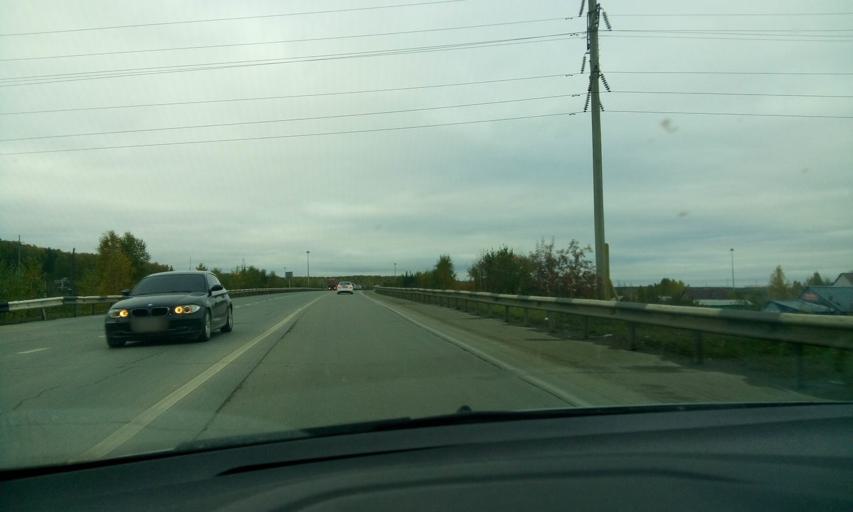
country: RU
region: Sverdlovsk
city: Istok
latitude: 56.7639
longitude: 60.7373
